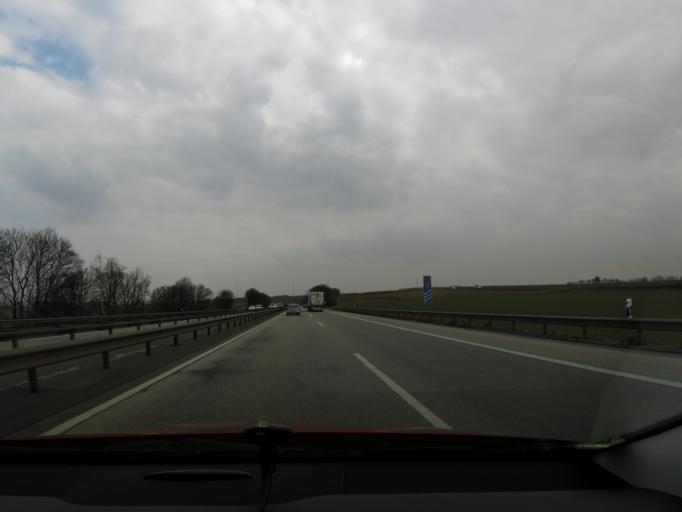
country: DE
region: Rheinland-Pfalz
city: Sprendlingen
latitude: 49.8448
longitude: 7.9863
